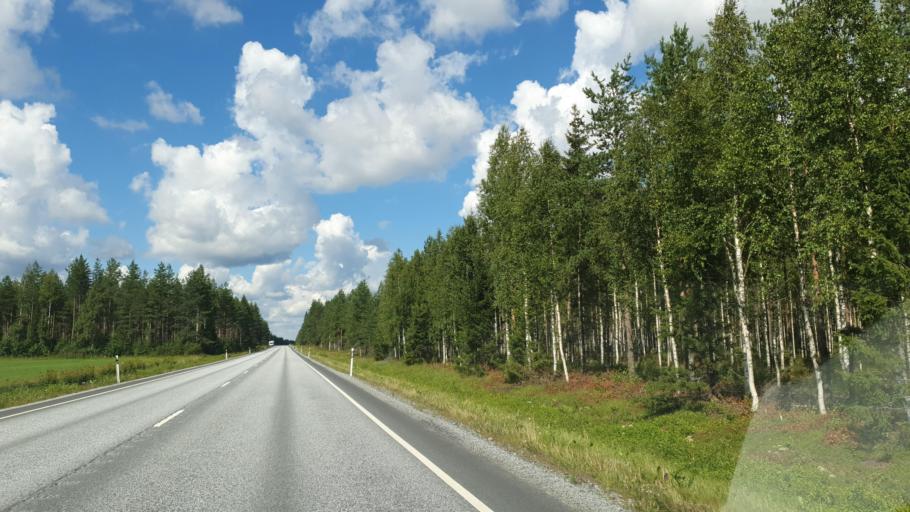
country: FI
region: Northern Savo
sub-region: Ylae-Savo
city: Sonkajaervi
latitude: 63.8919
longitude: 27.4208
